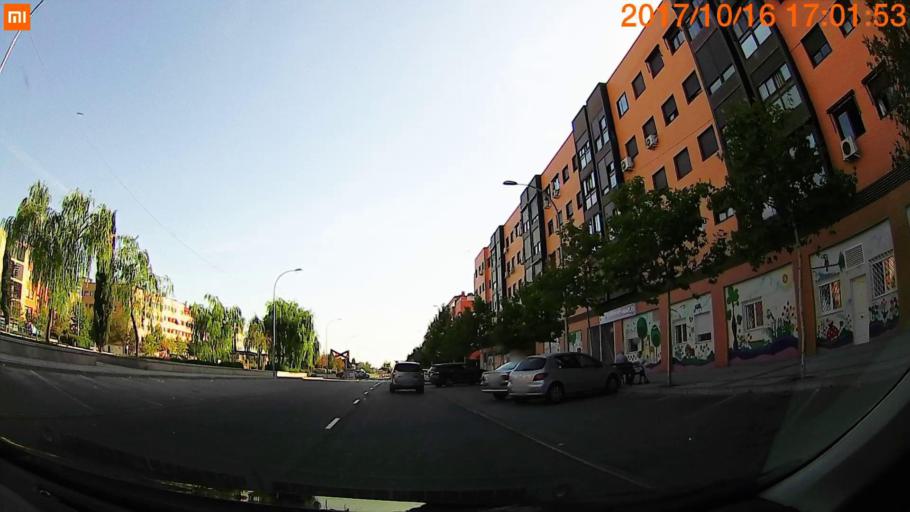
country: ES
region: Madrid
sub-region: Provincia de Madrid
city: Alcobendas
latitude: 40.5570
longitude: -3.6598
